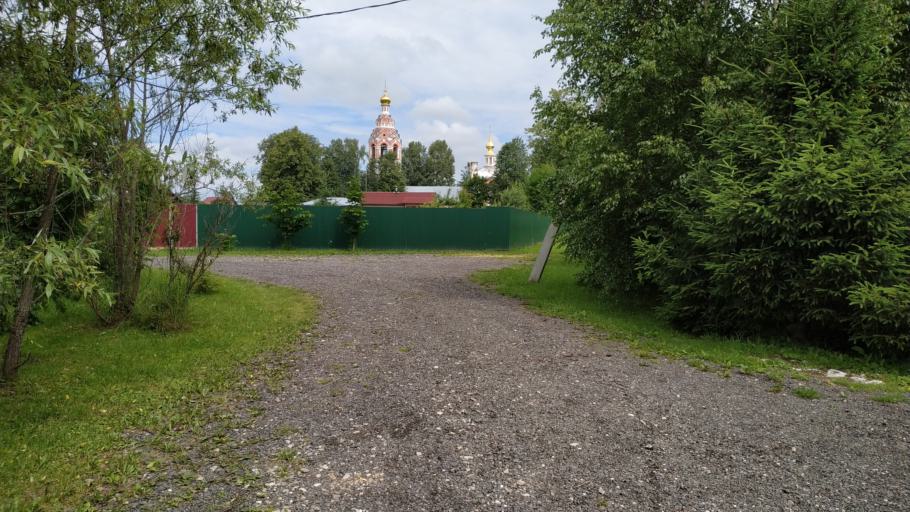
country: RU
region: Moskovskaya
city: Dorokhovo
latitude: 55.5572
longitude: 36.3170
